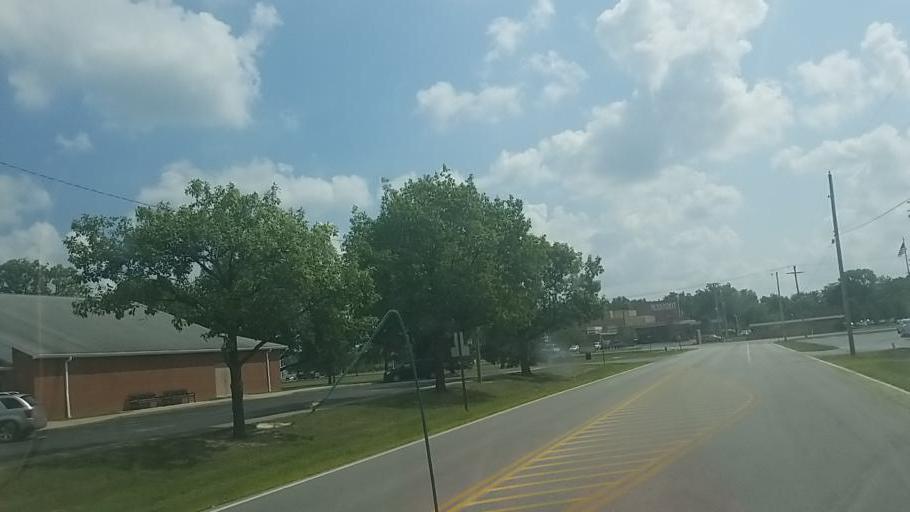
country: US
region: Ohio
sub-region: Wyandot County
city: Upper Sandusky
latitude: 40.8399
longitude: -83.2826
